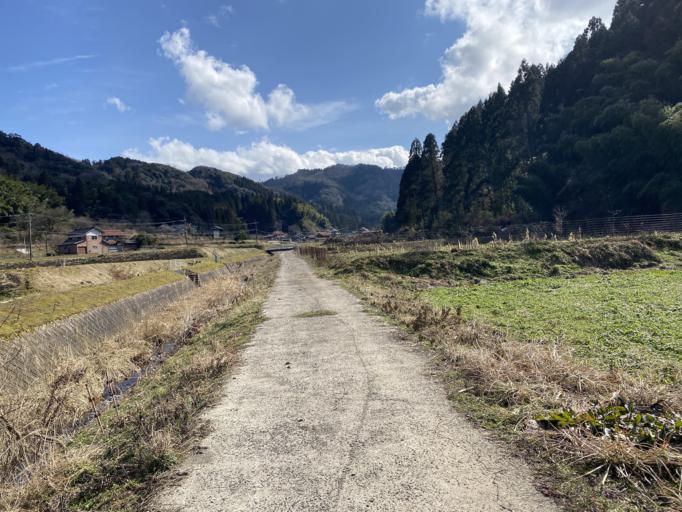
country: JP
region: Tottori
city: Kurayoshi
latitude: 35.4942
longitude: 133.9865
